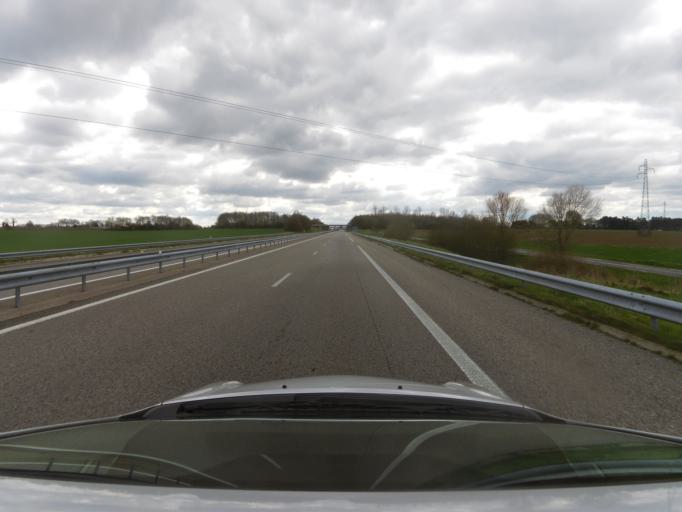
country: FR
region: Haute-Normandie
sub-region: Departement de la Seine-Maritime
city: Etainhus
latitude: 49.5627
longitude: 0.3409
